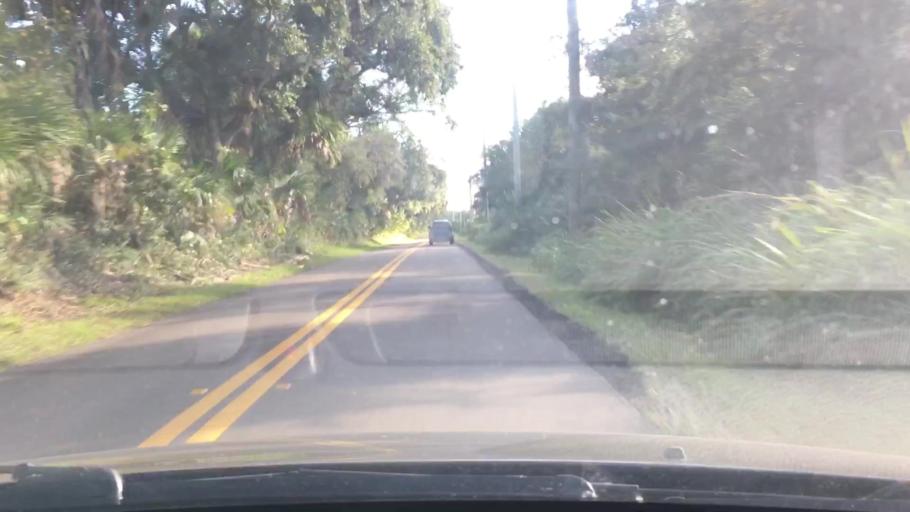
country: US
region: Florida
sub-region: Volusia County
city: Ormond-by-the-Sea
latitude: 29.3962
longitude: -81.0925
